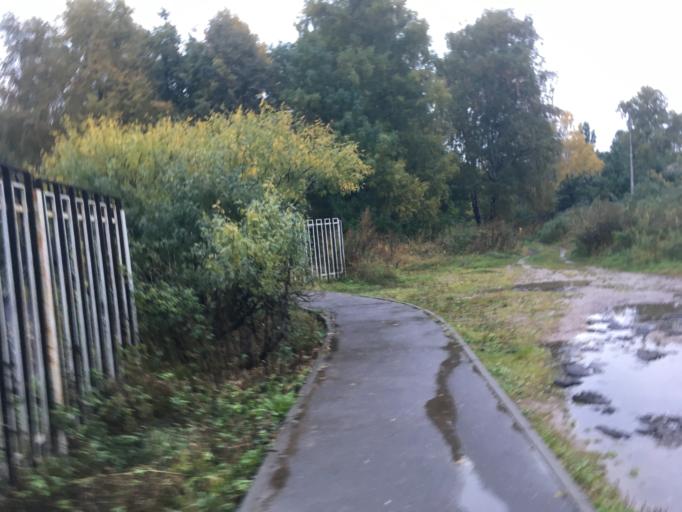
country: RU
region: Moskovskaya
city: Lyubertsy
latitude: 55.6946
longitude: 37.8792
